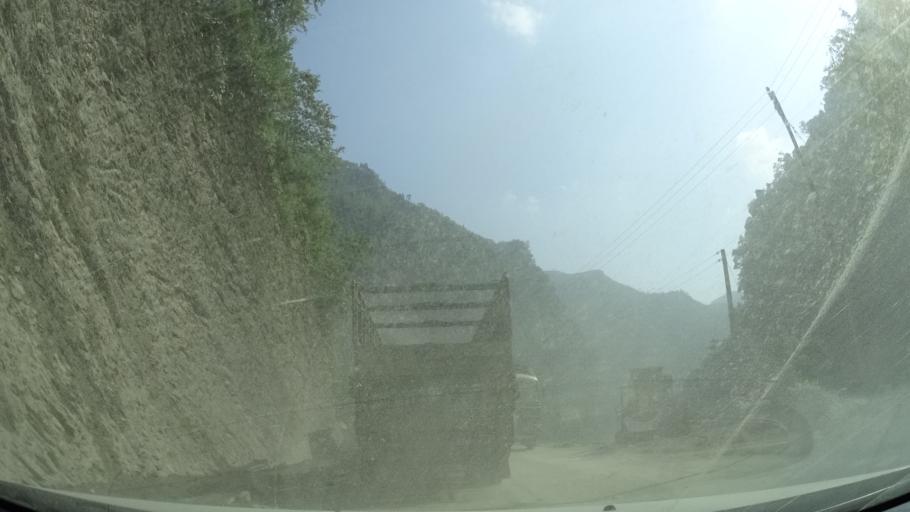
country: NP
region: Central Region
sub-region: Narayani Zone
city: Bharatpur
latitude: 27.8268
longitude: 84.5211
